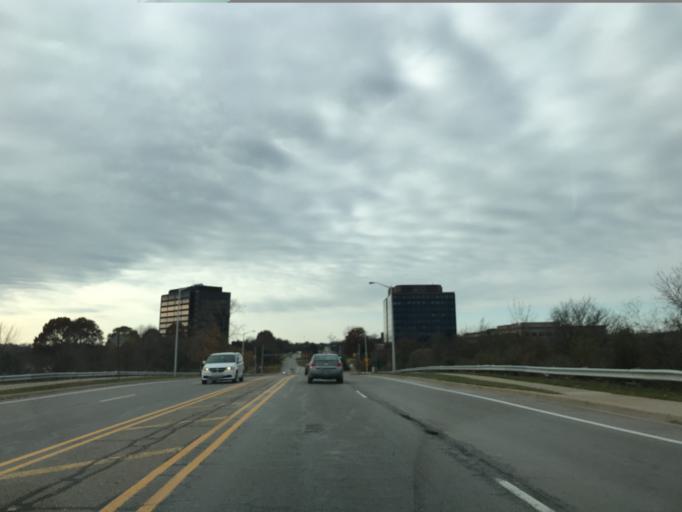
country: US
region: Michigan
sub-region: Washtenaw County
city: Ann Arbor
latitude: 42.2442
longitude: -83.7322
